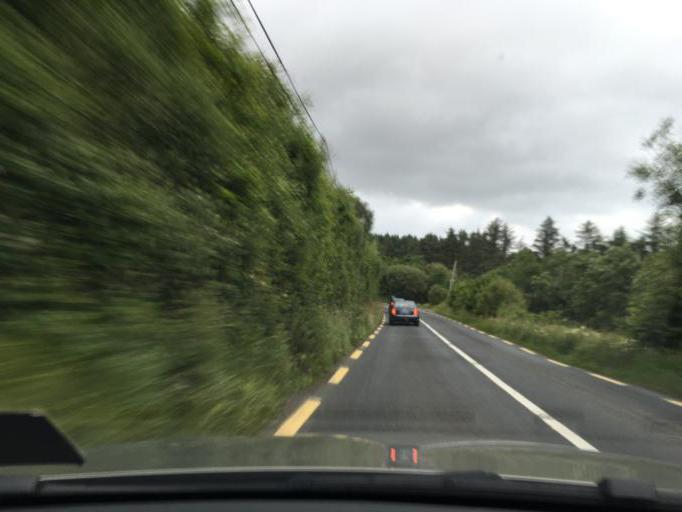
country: IE
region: Ulster
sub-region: County Donegal
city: Carndonagh
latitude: 55.2435
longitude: -7.3883
